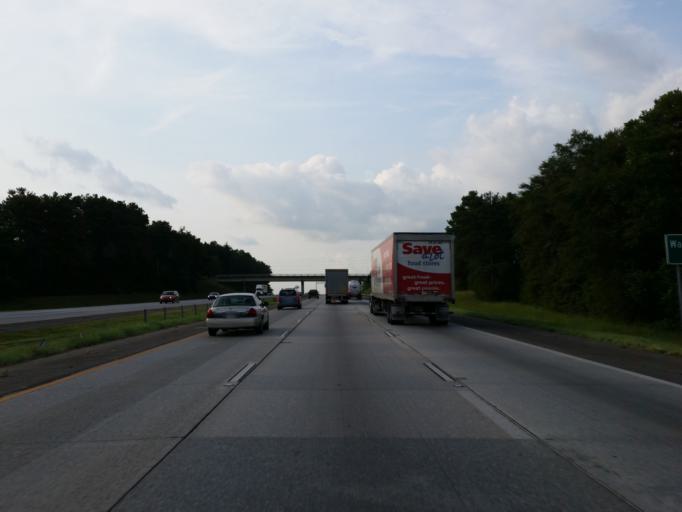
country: US
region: Georgia
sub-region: Houston County
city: Centerville
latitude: 32.5758
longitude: -83.7435
